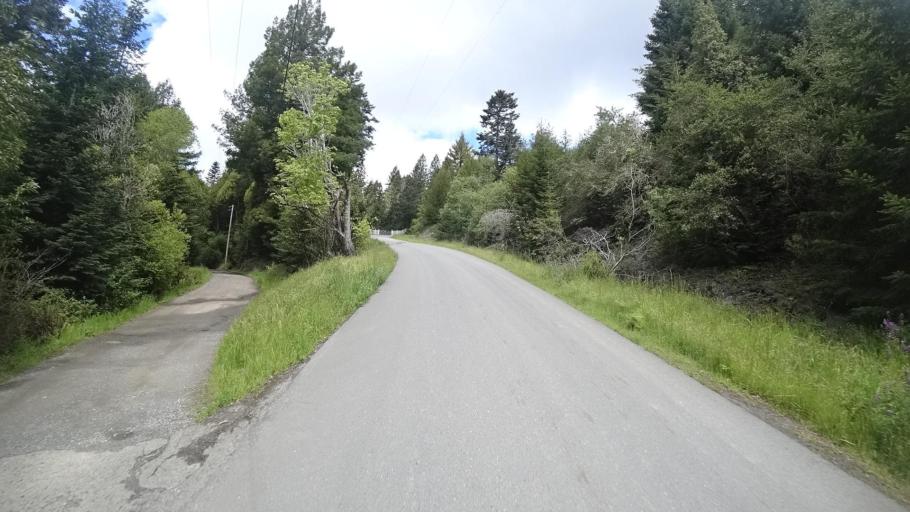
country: US
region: California
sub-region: Humboldt County
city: Blue Lake
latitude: 40.9032
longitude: -123.9863
